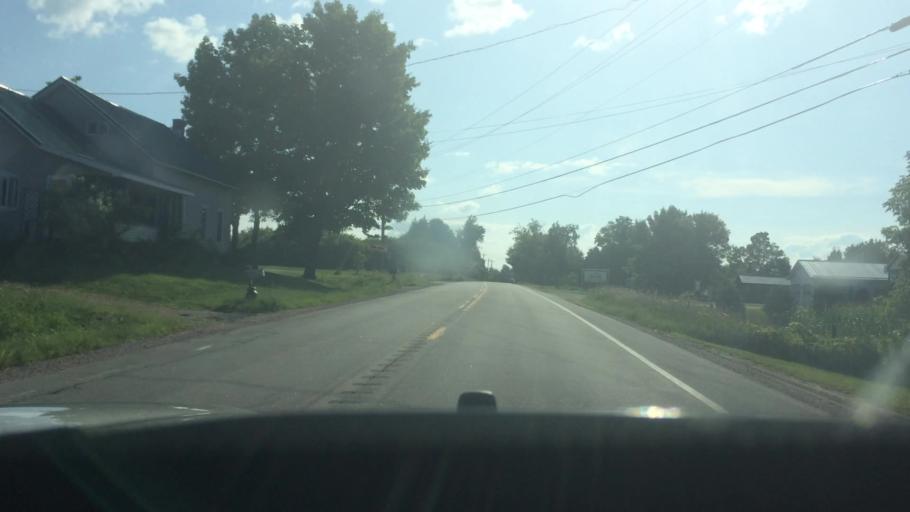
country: US
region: New York
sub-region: Franklin County
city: Malone
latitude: 44.7983
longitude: -74.4554
